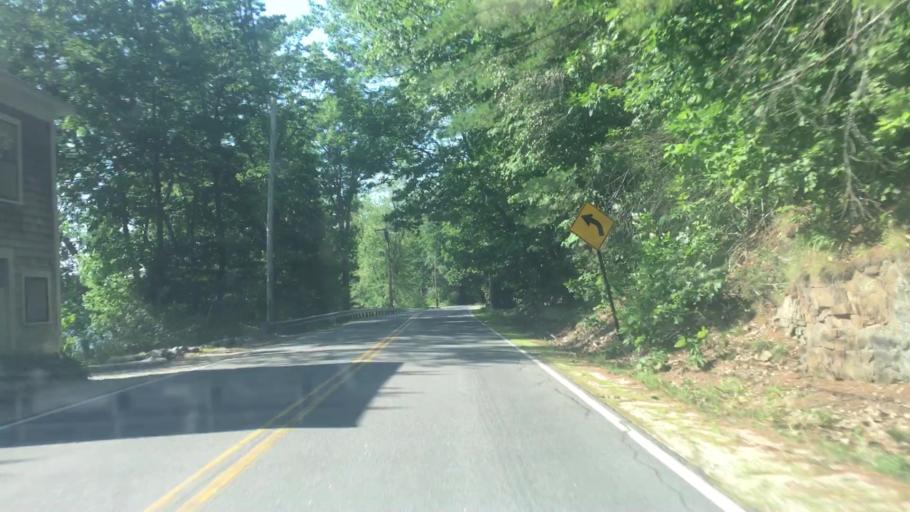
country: US
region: Maine
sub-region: York County
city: Hollis Center
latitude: 43.6626
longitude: -70.5982
